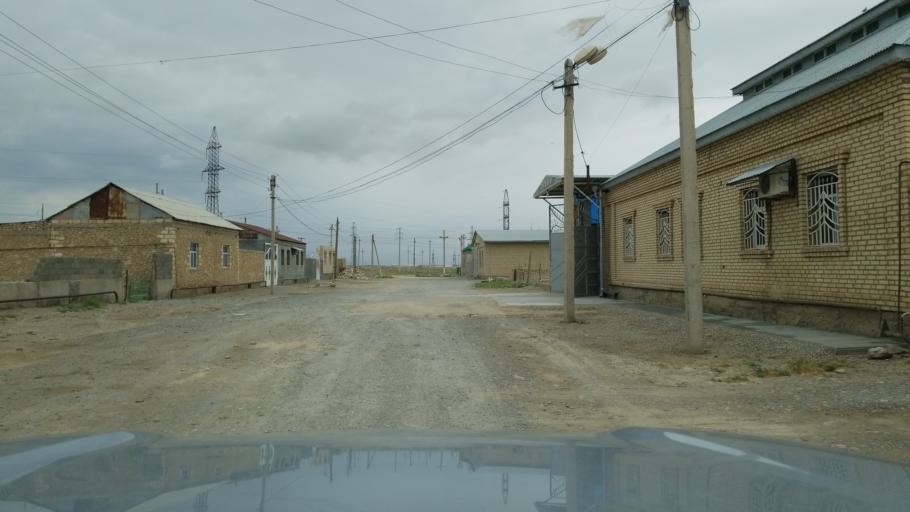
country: TM
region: Balkan
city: Serdar
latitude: 38.9680
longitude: 56.2606
